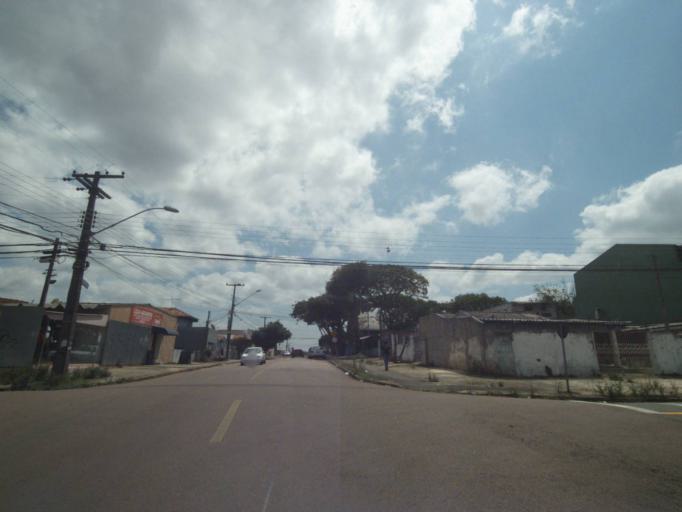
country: BR
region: Parana
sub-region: Curitiba
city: Curitiba
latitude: -25.5024
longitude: -49.3027
